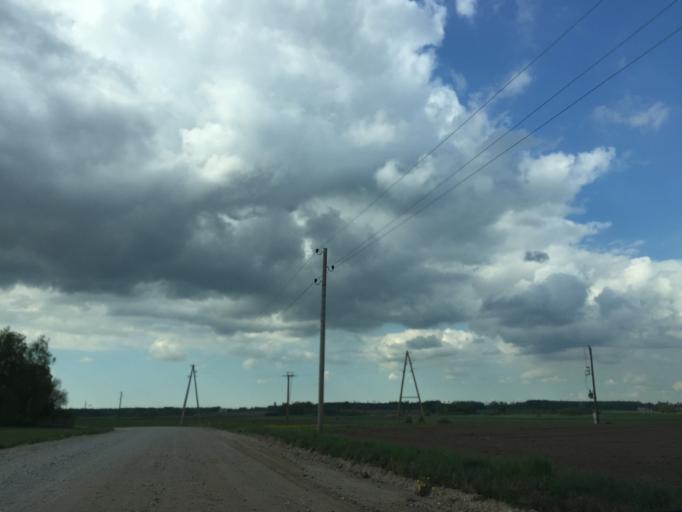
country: LV
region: Krimulda
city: Ragana
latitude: 57.2932
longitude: 24.7852
